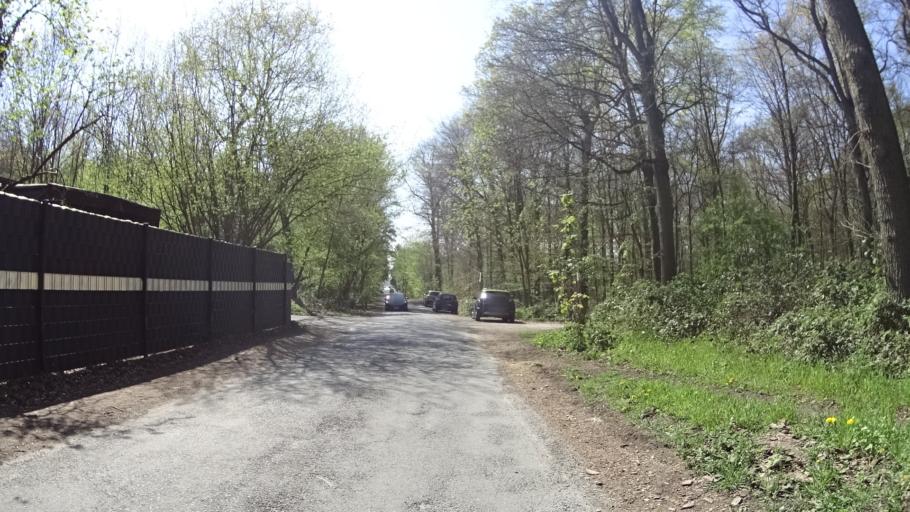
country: DE
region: North Rhine-Westphalia
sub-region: Regierungsbezirk Dusseldorf
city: Moers
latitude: 51.4005
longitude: 6.6325
